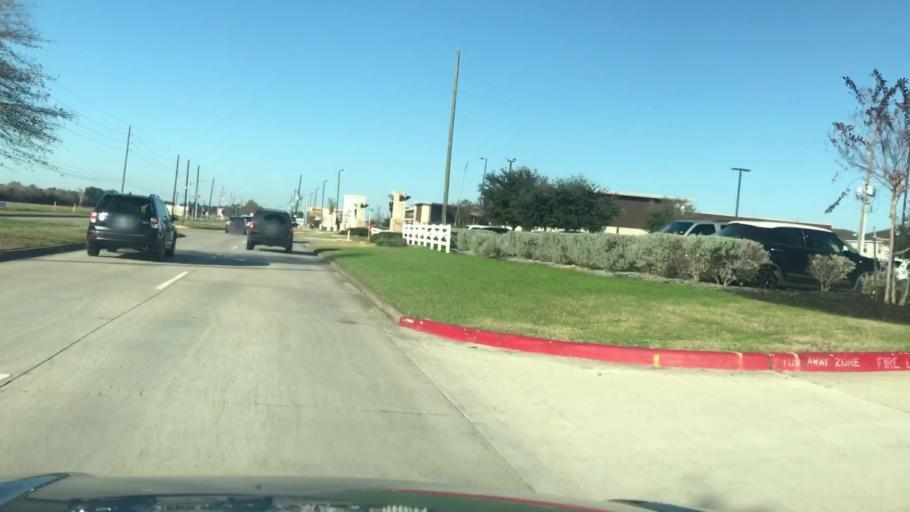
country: US
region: Texas
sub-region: Fort Bend County
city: Cinco Ranch
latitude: 29.8107
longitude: -95.7520
